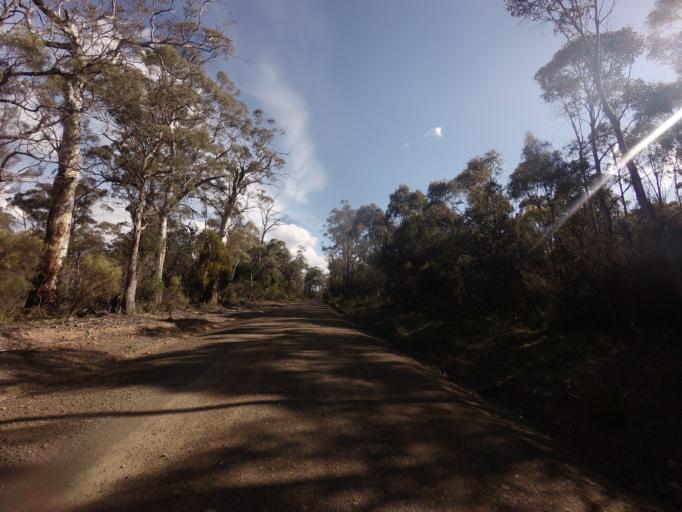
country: AU
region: Tasmania
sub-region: Break O'Day
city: St Helens
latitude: -41.8394
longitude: 148.0158
